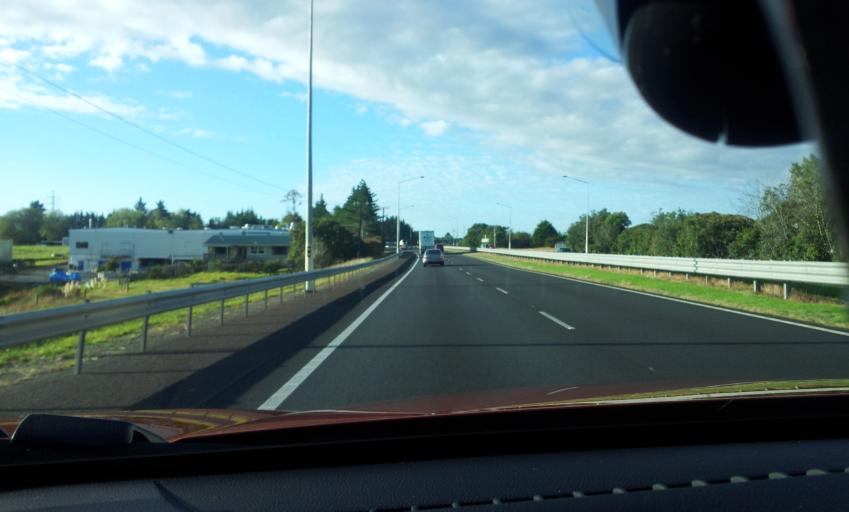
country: NZ
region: Auckland
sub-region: Auckland
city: Papakura
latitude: -37.1125
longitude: 174.9477
